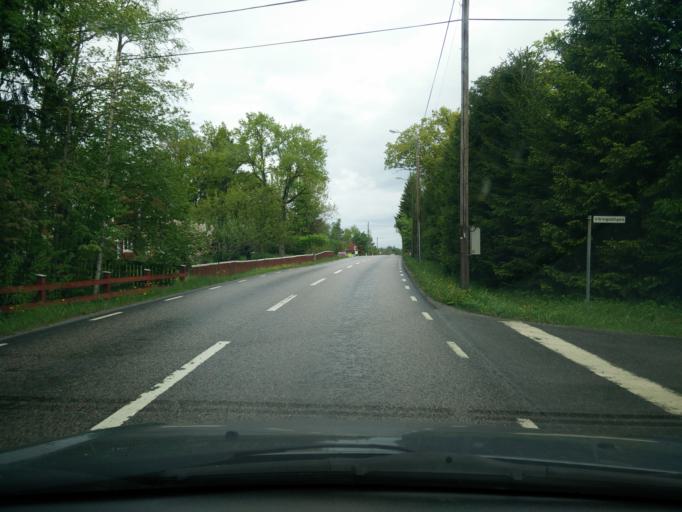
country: SE
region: Stockholm
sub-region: Norrtalje Kommun
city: Bjorko
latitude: 59.8121
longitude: 18.8933
